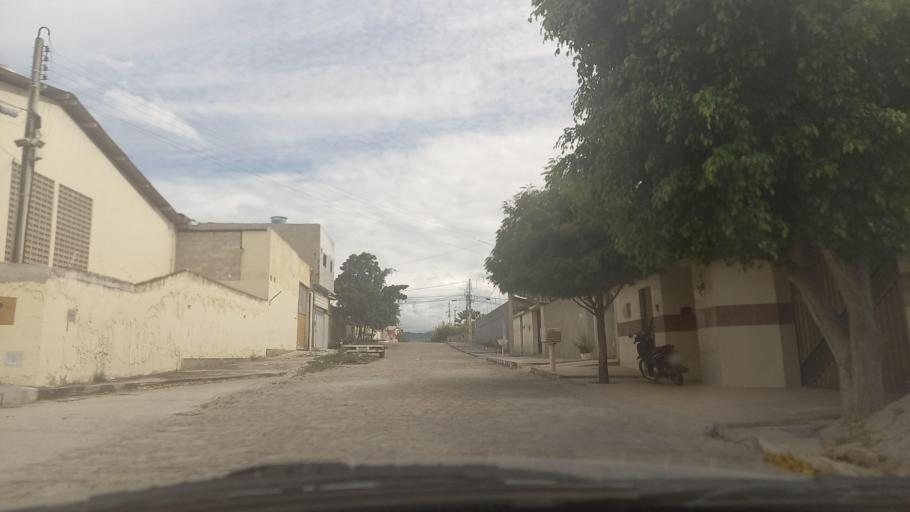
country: BR
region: Pernambuco
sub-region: Caruaru
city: Caruaru
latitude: -8.2906
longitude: -35.9900
